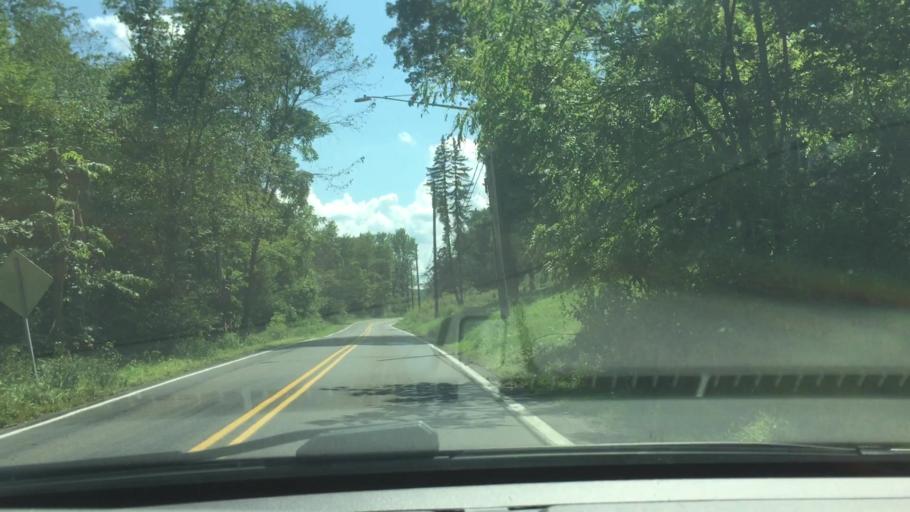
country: US
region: Pennsylvania
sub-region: Lawrence County
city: New Wilmington
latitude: 41.1112
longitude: -80.4379
